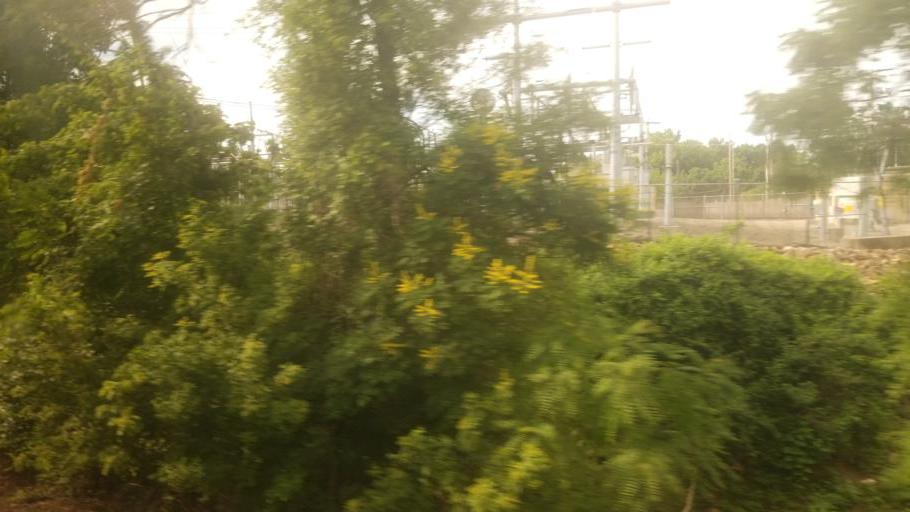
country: US
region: Kansas
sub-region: Douglas County
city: Lawrence
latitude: 38.9742
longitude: -95.2380
